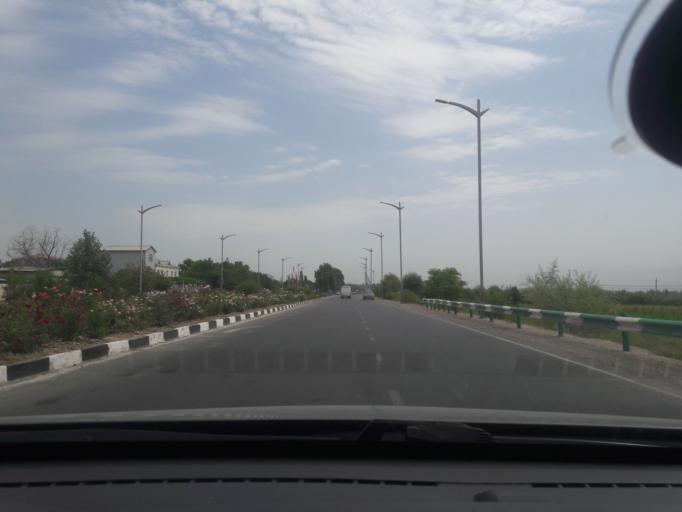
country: TJ
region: Republican Subordination
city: Hisor
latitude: 38.5523
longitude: 68.5931
